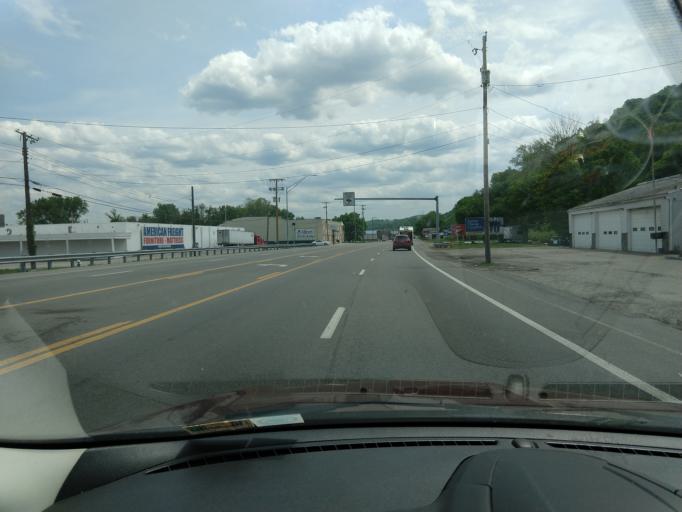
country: US
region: West Virginia
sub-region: Kanawha County
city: Dunbar
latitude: 38.3688
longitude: -81.7664
